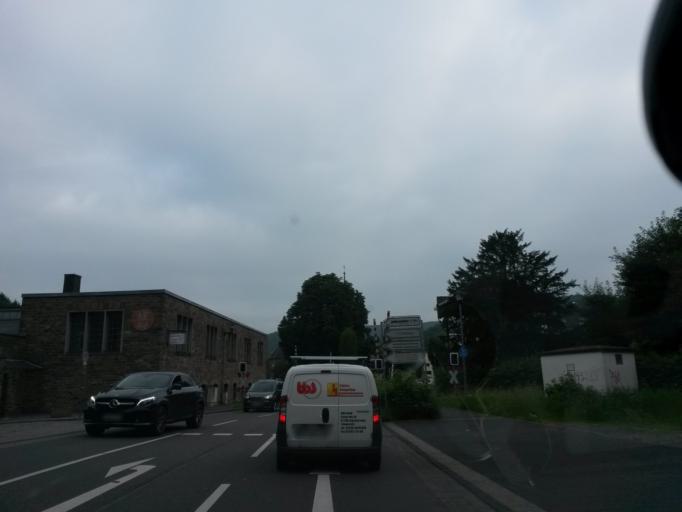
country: DE
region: North Rhine-Westphalia
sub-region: Regierungsbezirk Koln
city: Engelskirchen
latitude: 50.9839
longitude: 7.4101
